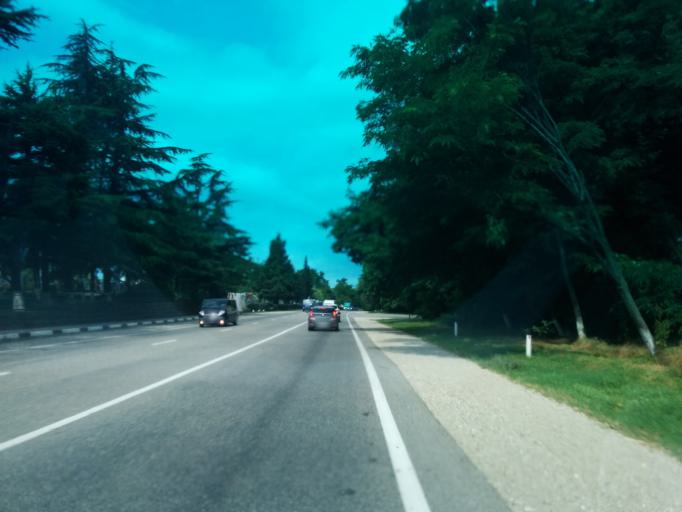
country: RU
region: Krasnodarskiy
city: Nebug
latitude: 44.1702
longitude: 38.9824
